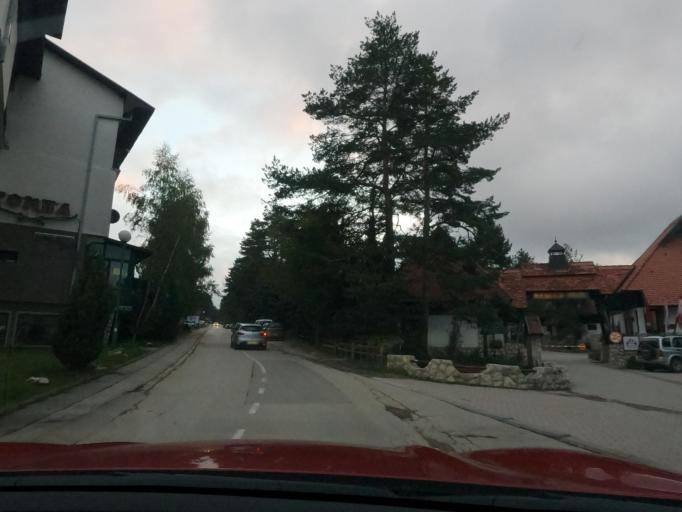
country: RS
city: Zlatibor
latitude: 43.7264
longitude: 19.7040
